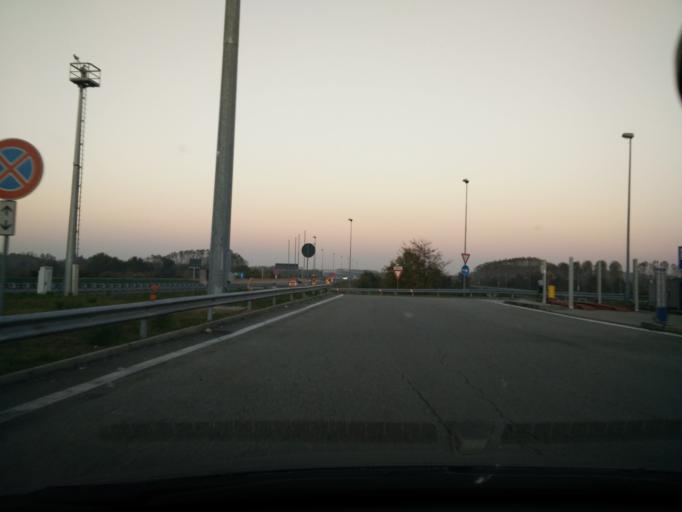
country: IT
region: Piedmont
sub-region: Provincia di Torino
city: Rondissone
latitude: 45.2420
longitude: 7.9737
